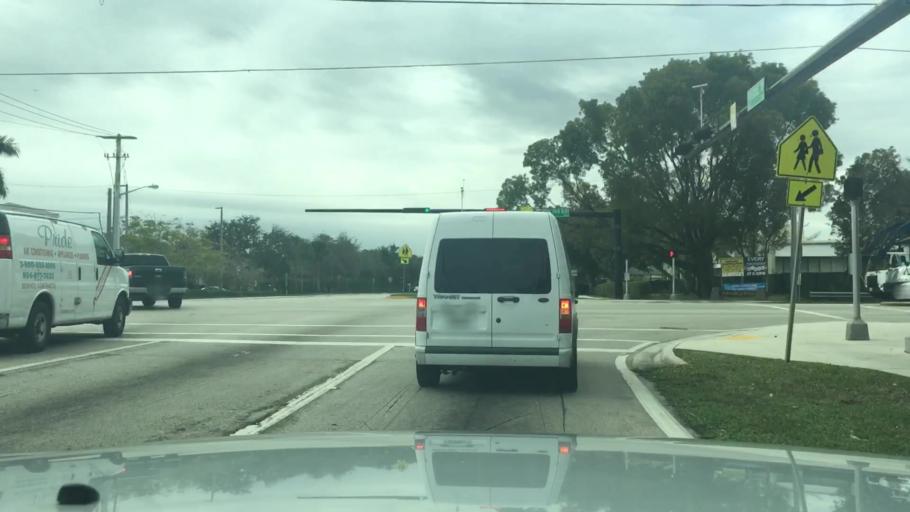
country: US
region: Florida
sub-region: Broward County
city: Margate
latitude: 26.2581
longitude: -80.2364
